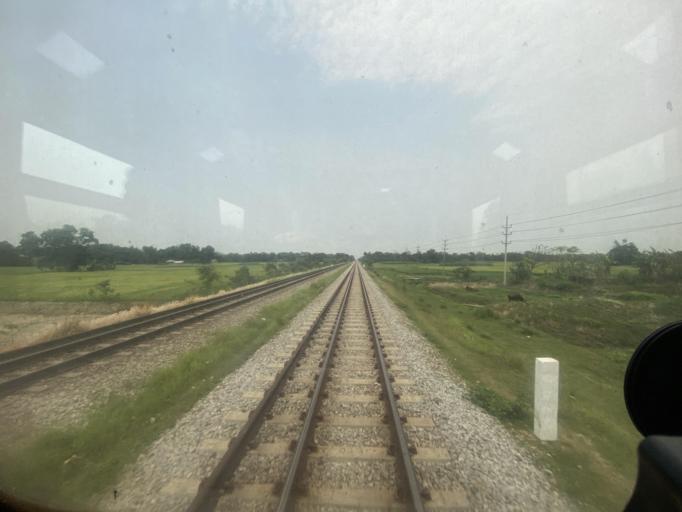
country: BD
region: Chittagong
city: Laksham
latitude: 23.3142
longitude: 91.1405
